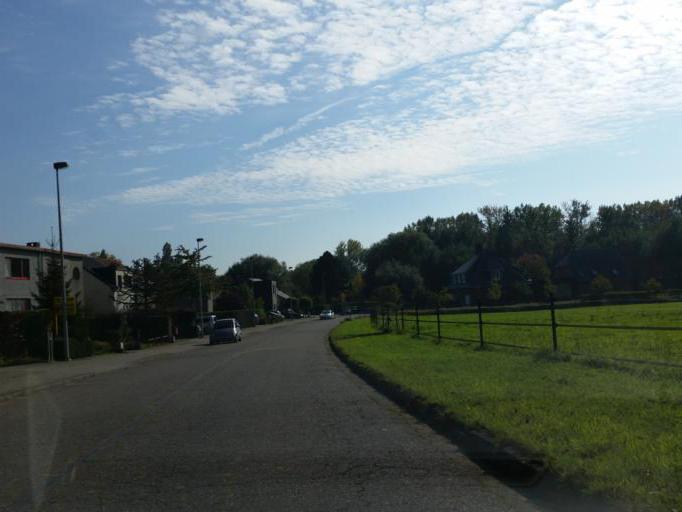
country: BE
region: Flanders
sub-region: Provincie Antwerpen
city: Edegem
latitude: 51.1616
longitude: 4.4107
